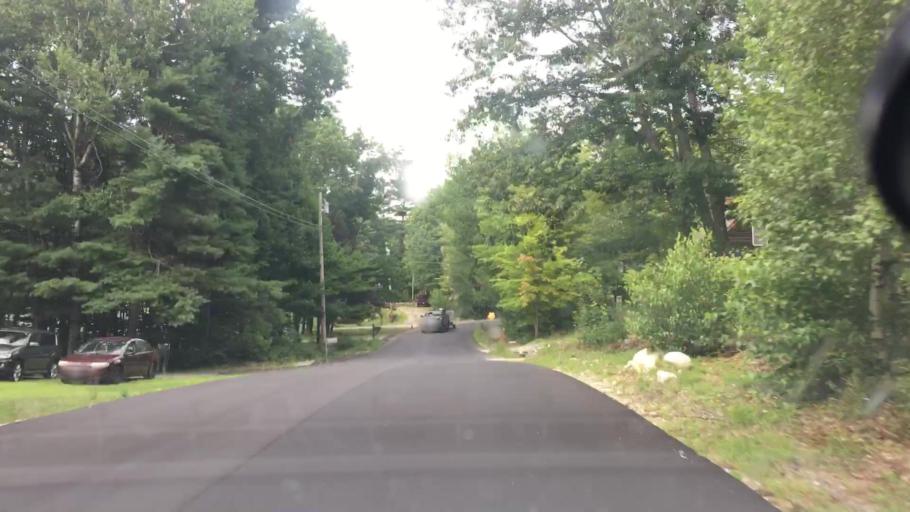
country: US
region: Maine
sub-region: Cumberland County
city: Raymond
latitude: 43.8866
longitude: -70.4591
